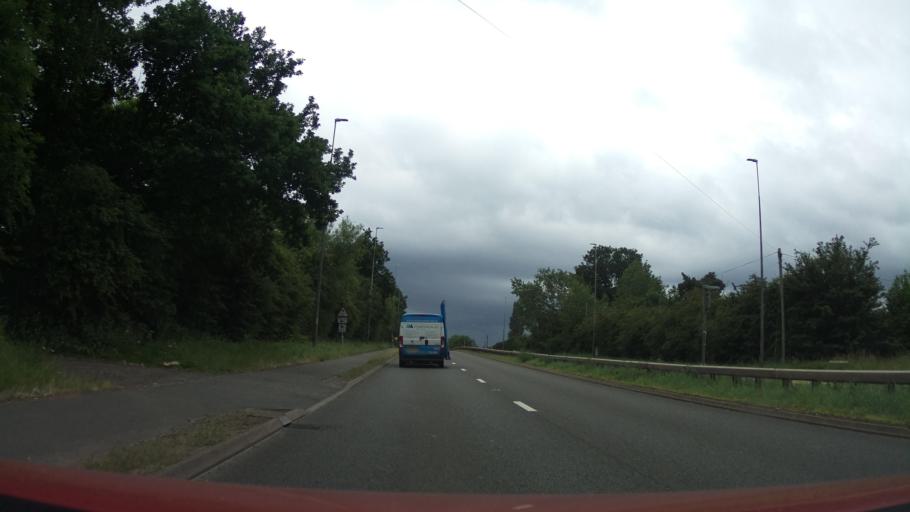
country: GB
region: England
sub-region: Staffordshire
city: Featherstone
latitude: 52.6474
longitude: -2.1281
